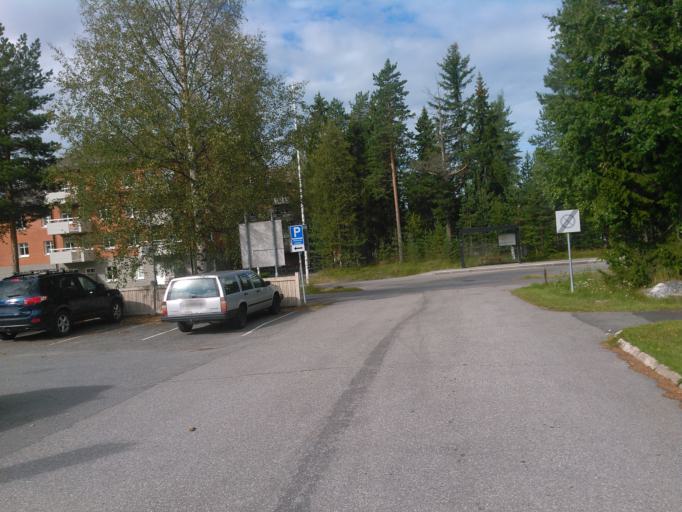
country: SE
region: Vaesterbotten
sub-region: Umea Kommun
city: Ersmark
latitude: 63.8258
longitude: 20.3275
